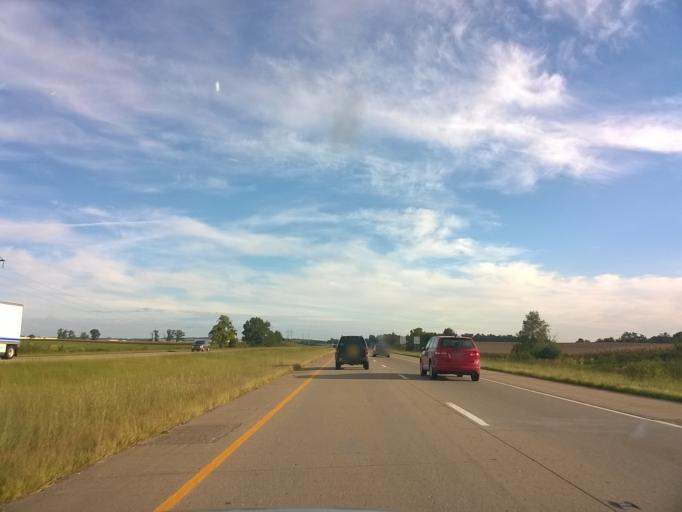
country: US
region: Indiana
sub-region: Vanderburgh County
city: Melody Hill
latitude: 38.1028
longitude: -87.4762
